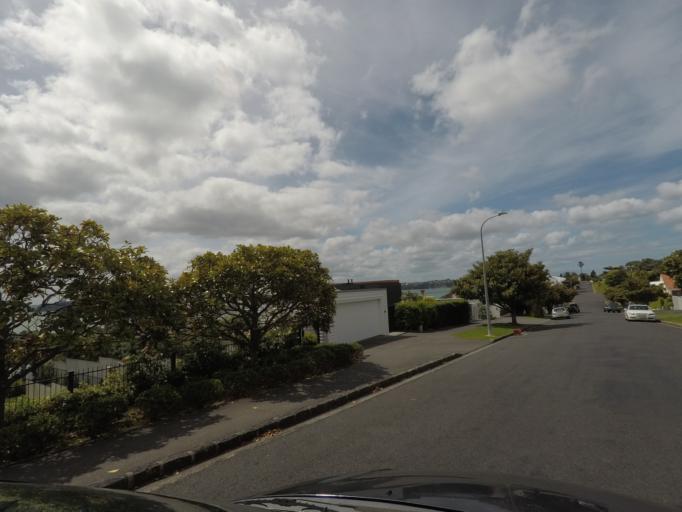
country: NZ
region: Auckland
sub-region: Auckland
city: Auckland
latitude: -36.8470
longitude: 174.7244
